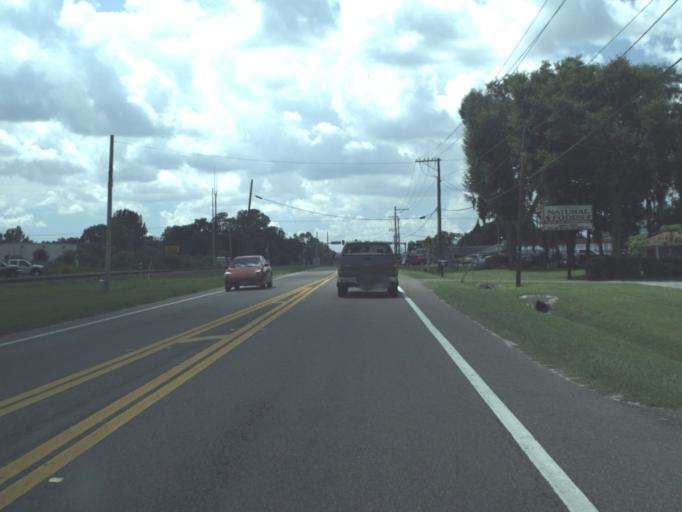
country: US
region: Florida
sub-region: Hillsborough County
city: Dover
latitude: 27.9981
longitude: -82.2048
